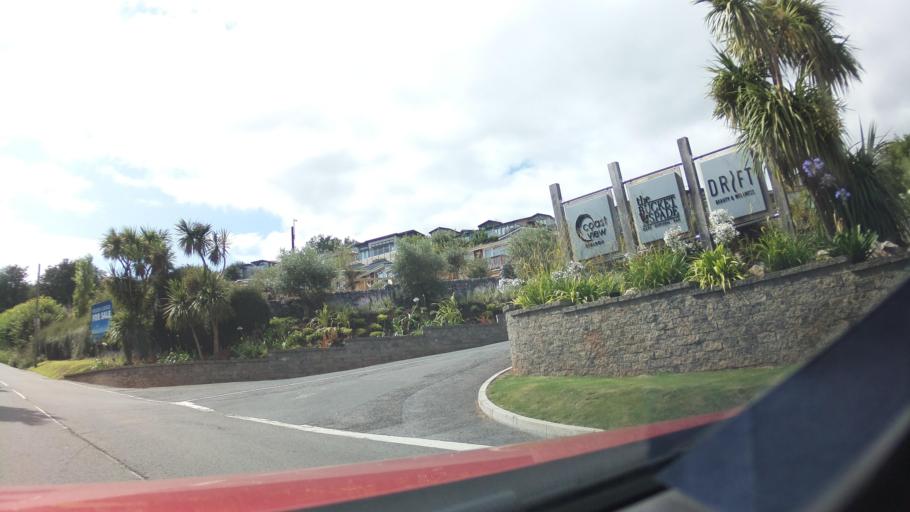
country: GB
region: England
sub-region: Devon
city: Teignmouth
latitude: 50.5348
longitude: -3.5028
